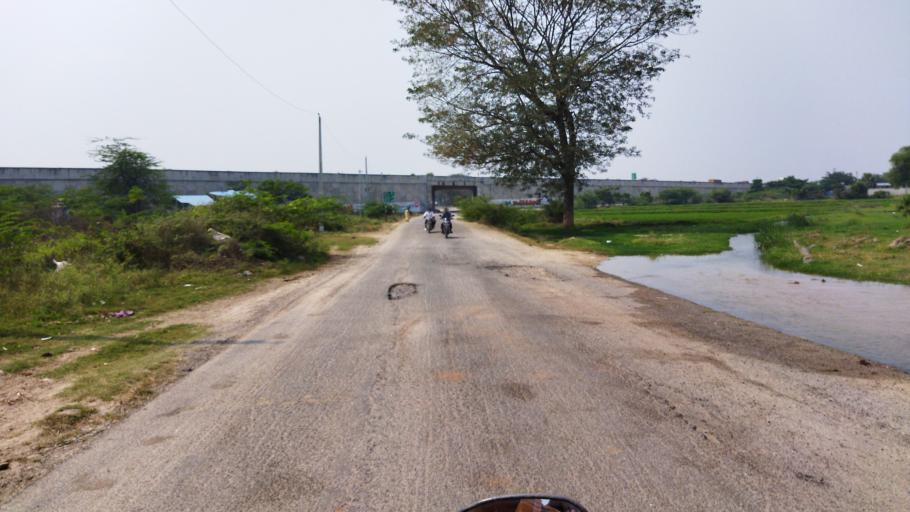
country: IN
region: Telangana
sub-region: Nalgonda
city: Nalgonda
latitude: 17.1596
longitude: 79.4202
